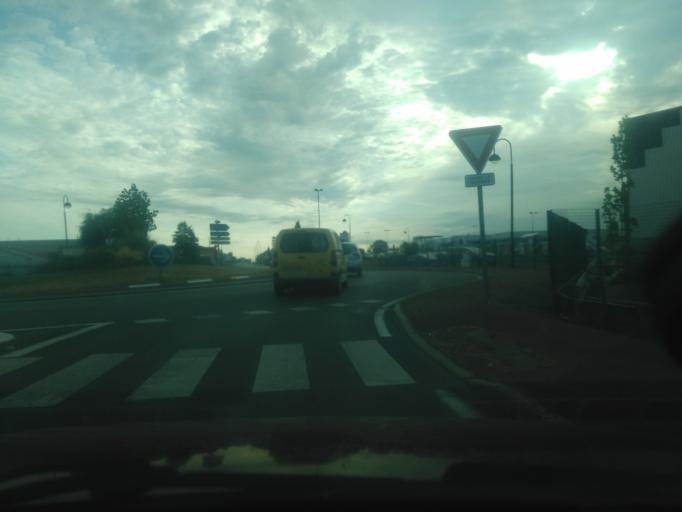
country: FR
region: Pays de la Loire
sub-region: Departement de la Vendee
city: Les Essarts
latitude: 46.7650
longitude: -1.2379
